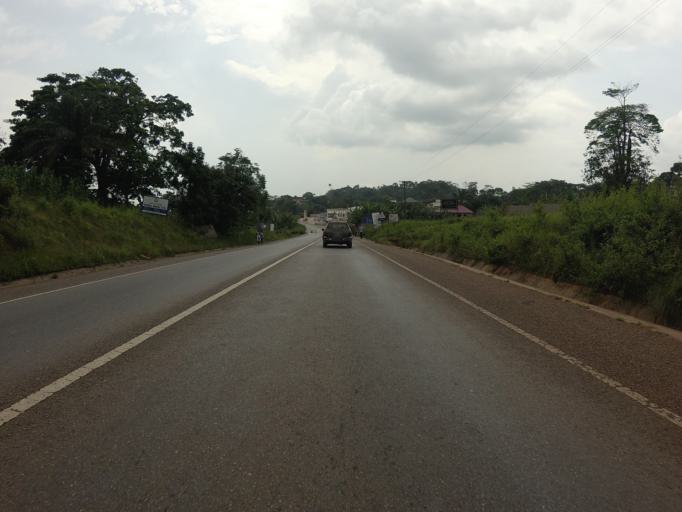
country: GH
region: Eastern
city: Aburi
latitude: 5.8579
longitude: -0.1676
